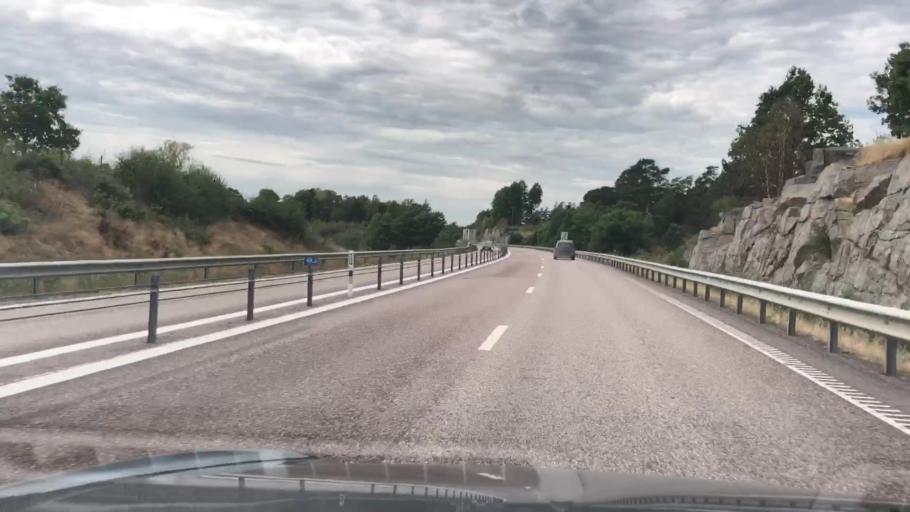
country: SE
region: Blekinge
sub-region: Ronneby Kommun
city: Brakne-Hoby
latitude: 56.2084
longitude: 15.0465
